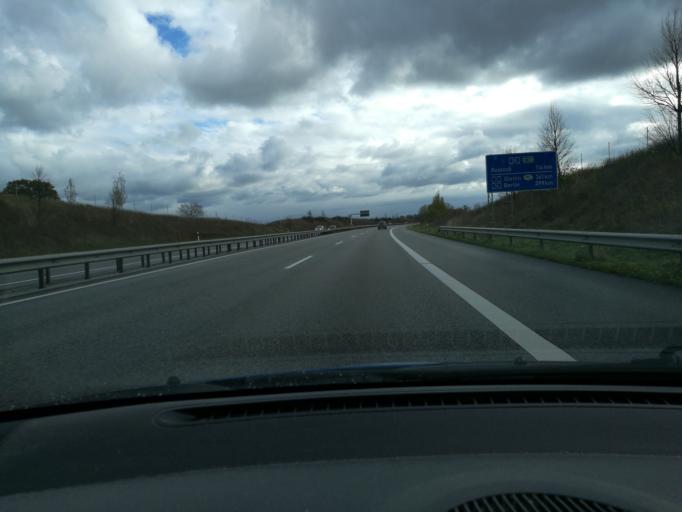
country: DE
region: Schleswig-Holstein
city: Krummesse
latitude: 53.8240
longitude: 10.6579
